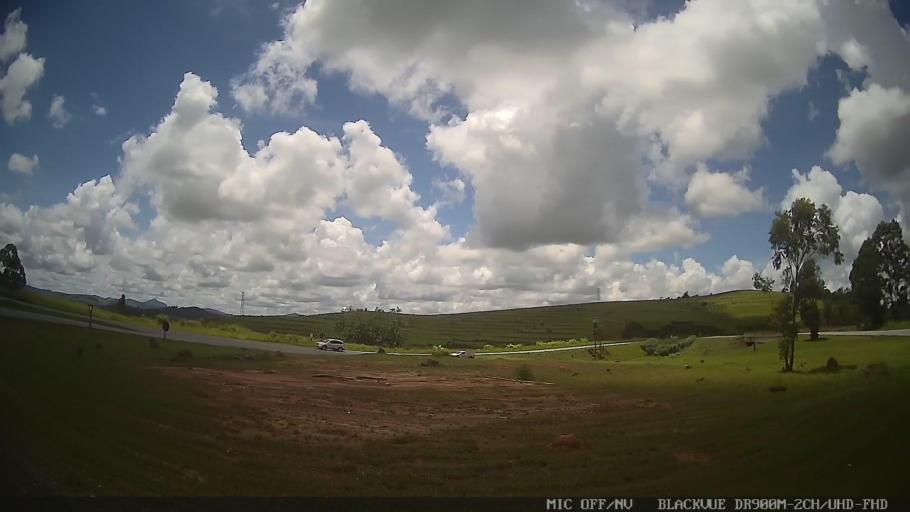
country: BR
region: Sao Paulo
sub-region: Amparo
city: Amparo
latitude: -22.7568
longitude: -46.7590
